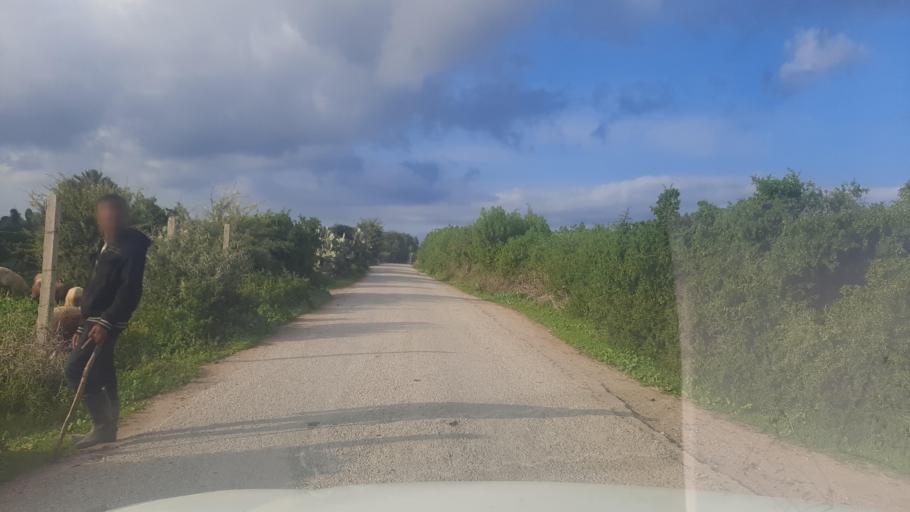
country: TN
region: Nabul
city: Manzil Bu Zalafah
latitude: 36.7108
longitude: 10.5007
